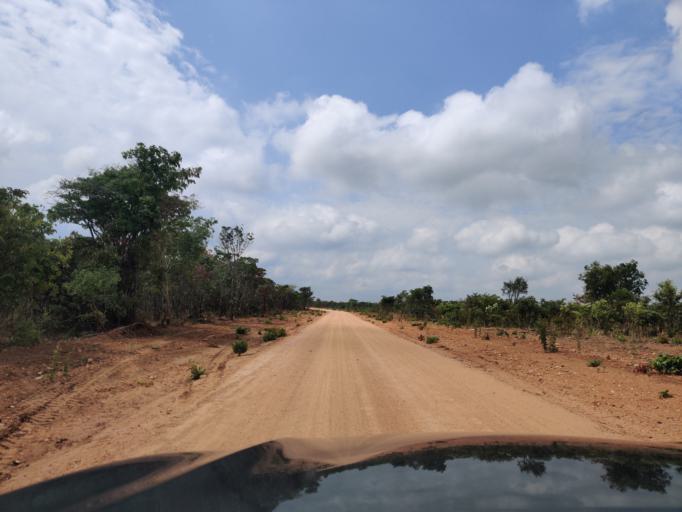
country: ZM
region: Central
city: Mkushi
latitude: -13.6625
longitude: 29.7516
